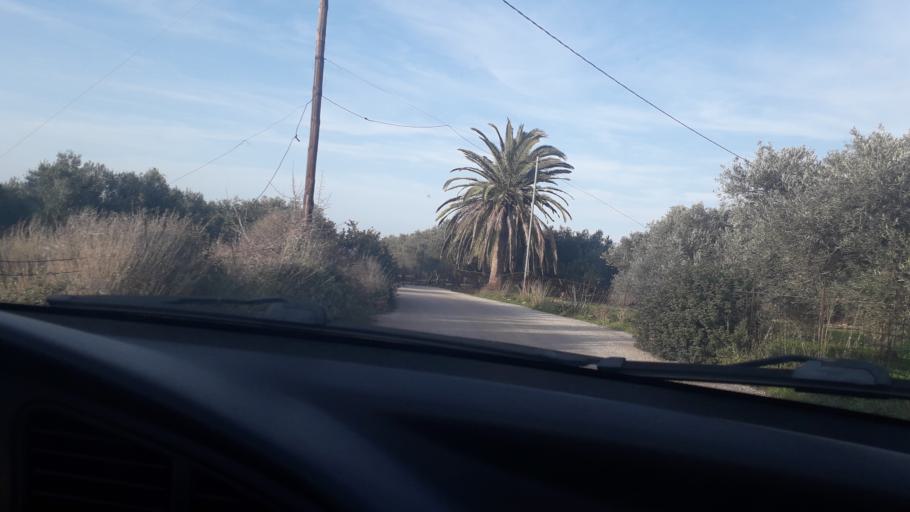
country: GR
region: Crete
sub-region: Nomos Rethymnis
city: Panormos
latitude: 35.3859
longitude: 24.6242
